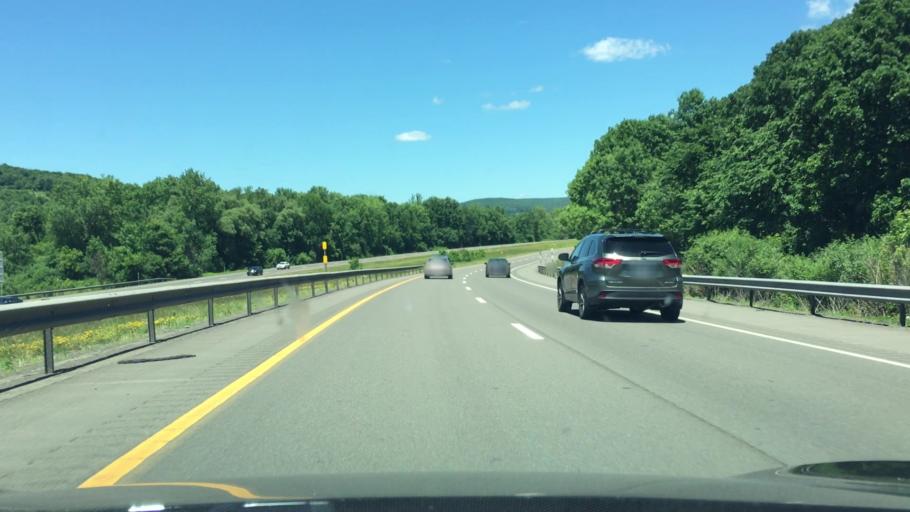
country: US
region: New York
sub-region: Cortland County
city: Homer
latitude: 42.6609
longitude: -76.1739
